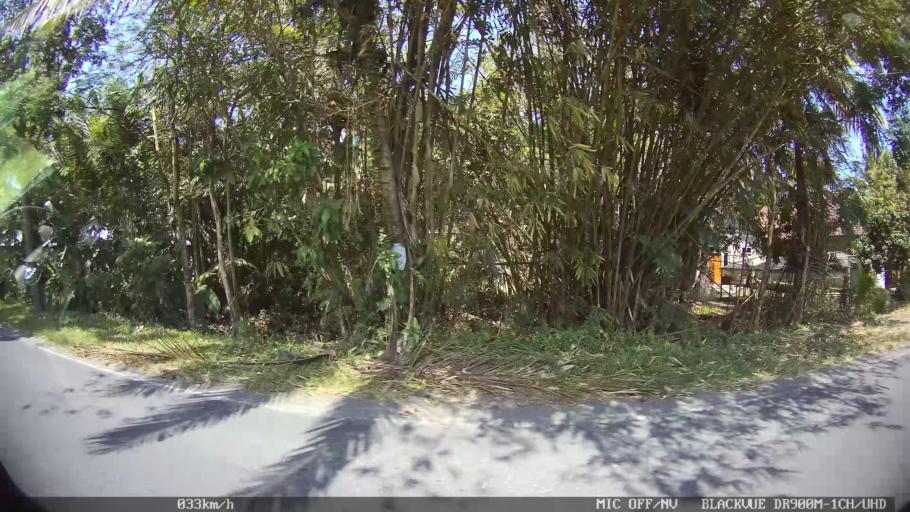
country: ID
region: Daerah Istimewa Yogyakarta
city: Srandakan
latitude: -7.9323
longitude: 110.1415
